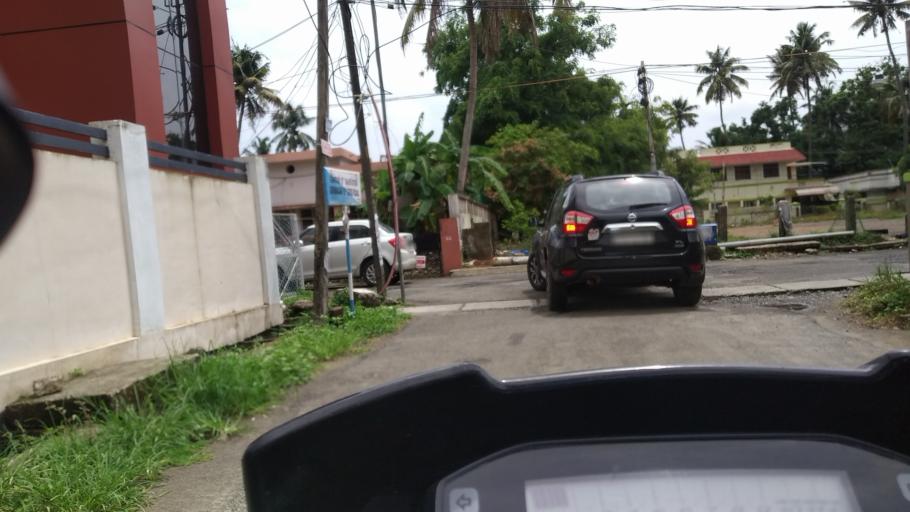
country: IN
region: Kerala
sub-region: Ernakulam
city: Cochin
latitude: 9.9618
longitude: 76.2991
